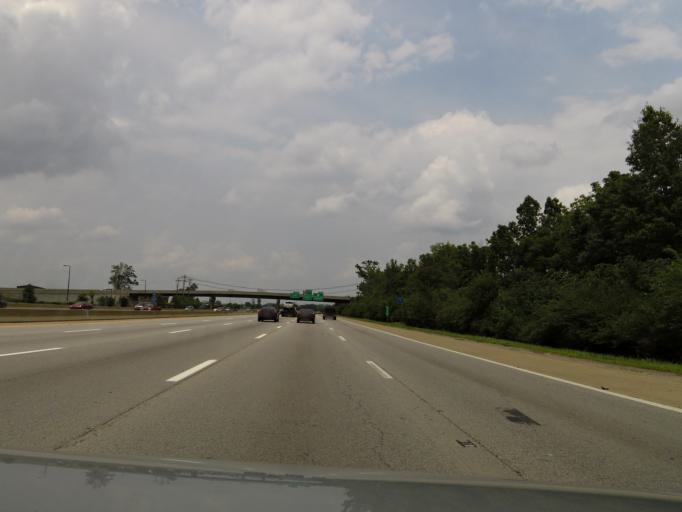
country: US
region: Kentucky
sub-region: Jefferson County
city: Audubon Park
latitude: 38.1671
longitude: -85.7206
